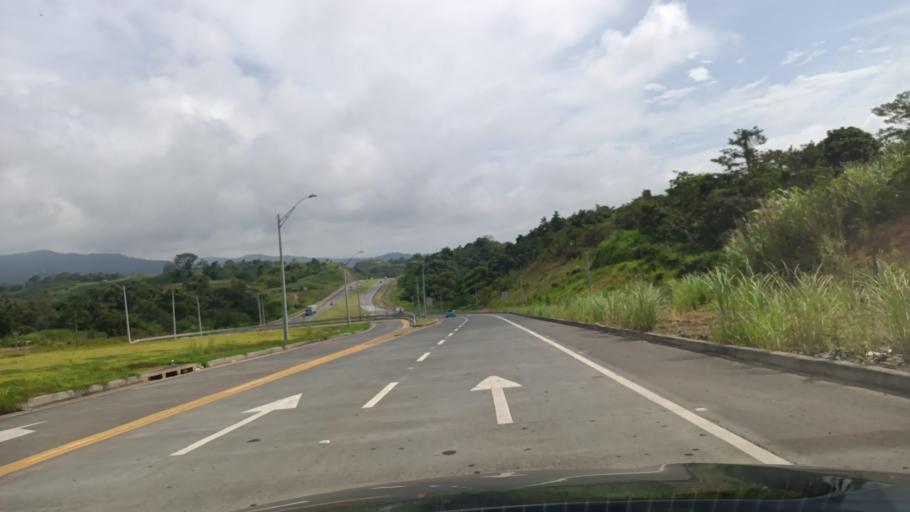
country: PA
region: Panama
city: Las Cumbres
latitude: 9.0963
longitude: -79.4850
